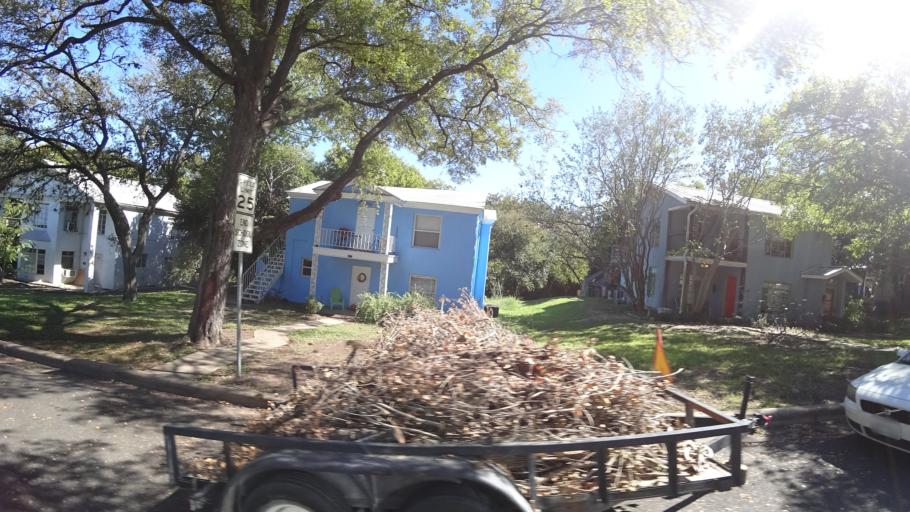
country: US
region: Texas
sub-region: Travis County
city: Austin
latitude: 30.2941
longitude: -97.7133
